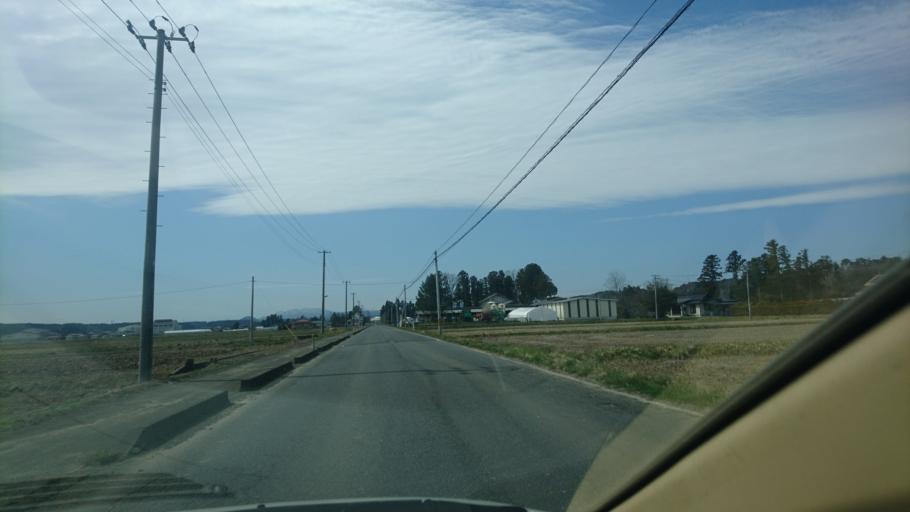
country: JP
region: Miyagi
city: Furukawa
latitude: 38.7401
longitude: 140.9679
